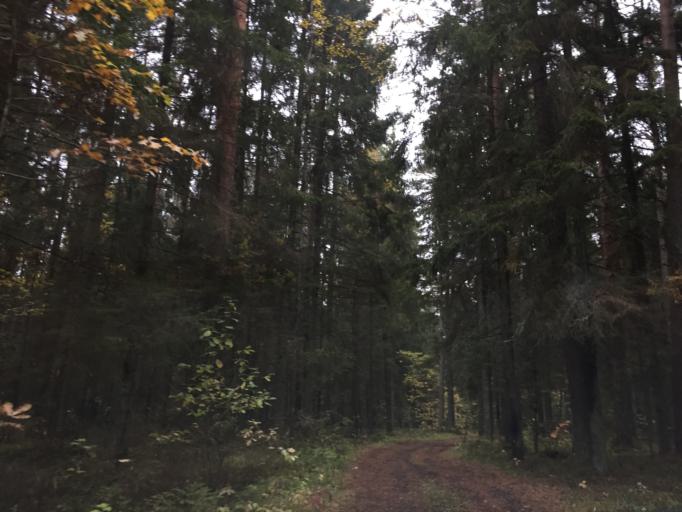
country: LV
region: Jelgava
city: Jelgava
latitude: 56.7342
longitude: 23.6900
